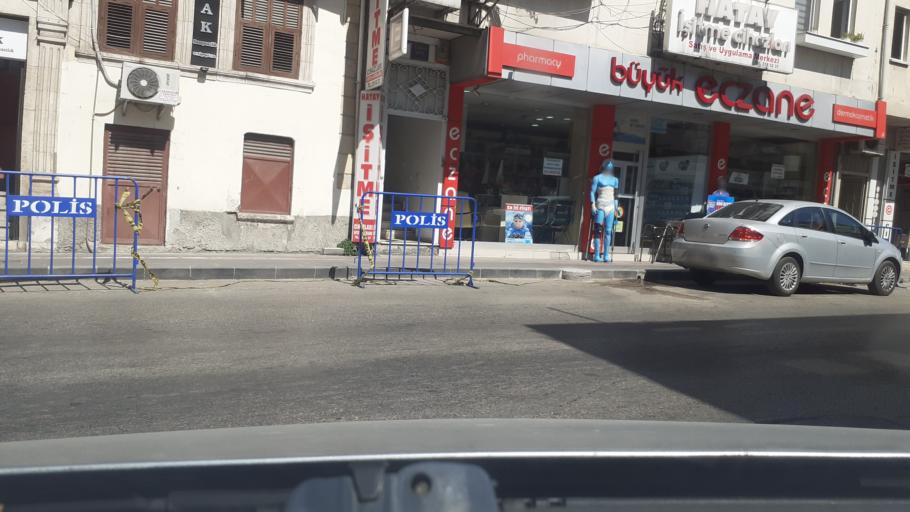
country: TR
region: Hatay
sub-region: Antakya Ilcesi
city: Antakya
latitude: 36.1973
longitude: 36.1616
